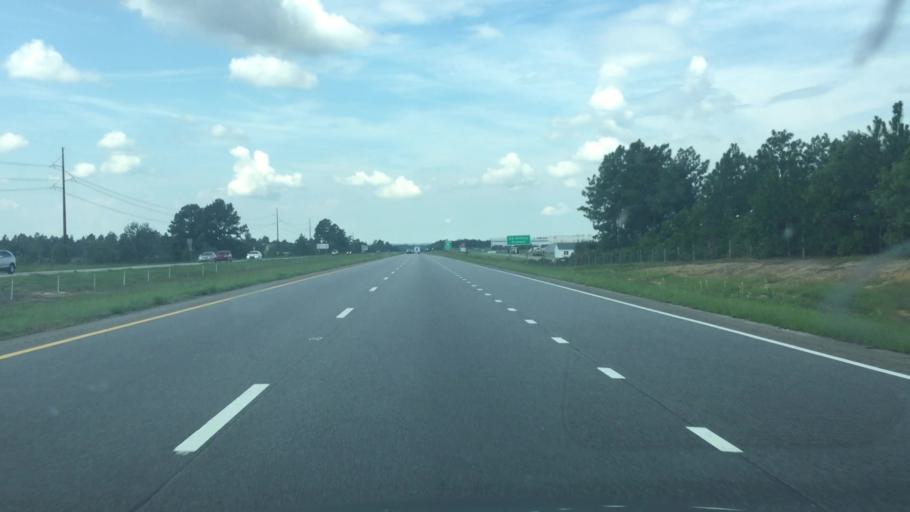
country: US
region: North Carolina
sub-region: Richmond County
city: Hamlet
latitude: 34.8555
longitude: -79.7007
